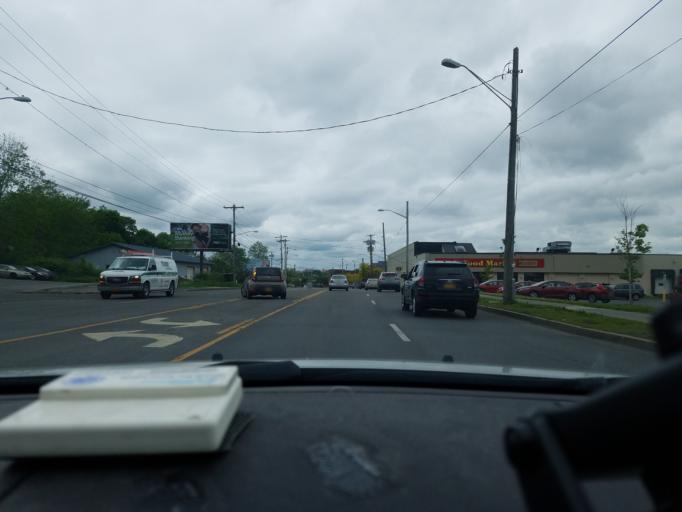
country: US
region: New York
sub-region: Onondaga County
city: Syracuse
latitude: 43.0497
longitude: -76.1249
